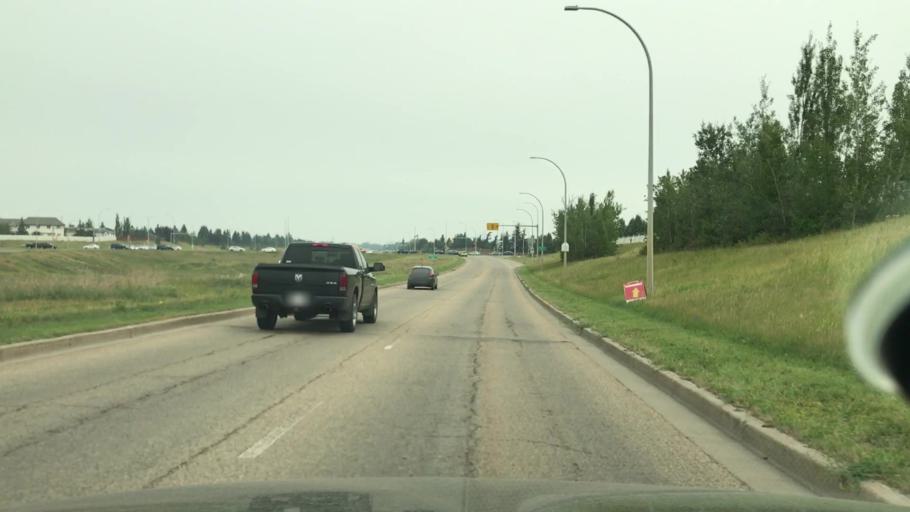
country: CA
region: Alberta
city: Edmonton
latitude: 53.4661
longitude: -113.5830
